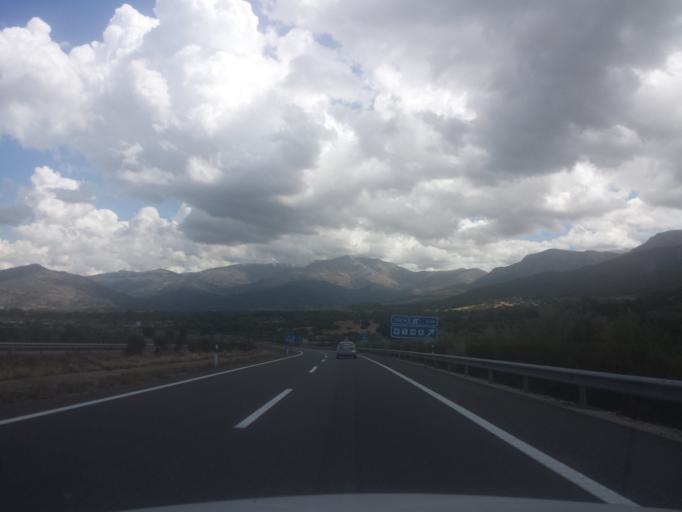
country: ES
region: Extremadura
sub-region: Provincia de Caceres
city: Aldeanueva del Camino
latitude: 40.2562
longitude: -5.9257
